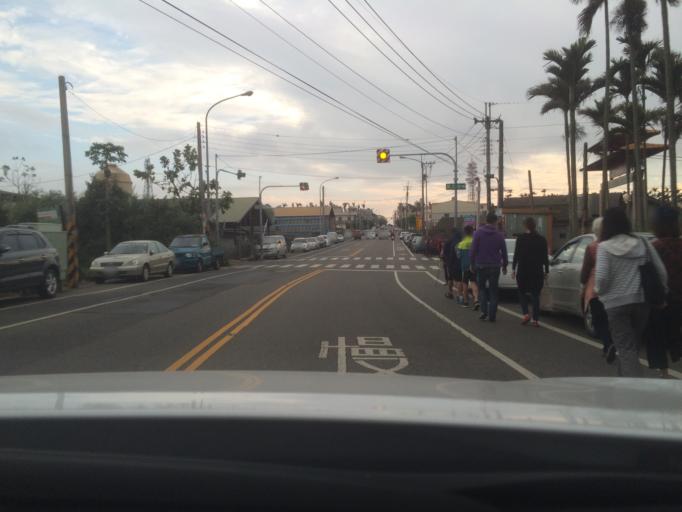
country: TW
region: Taiwan
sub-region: Nantou
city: Nantou
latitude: 23.9297
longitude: 120.6390
